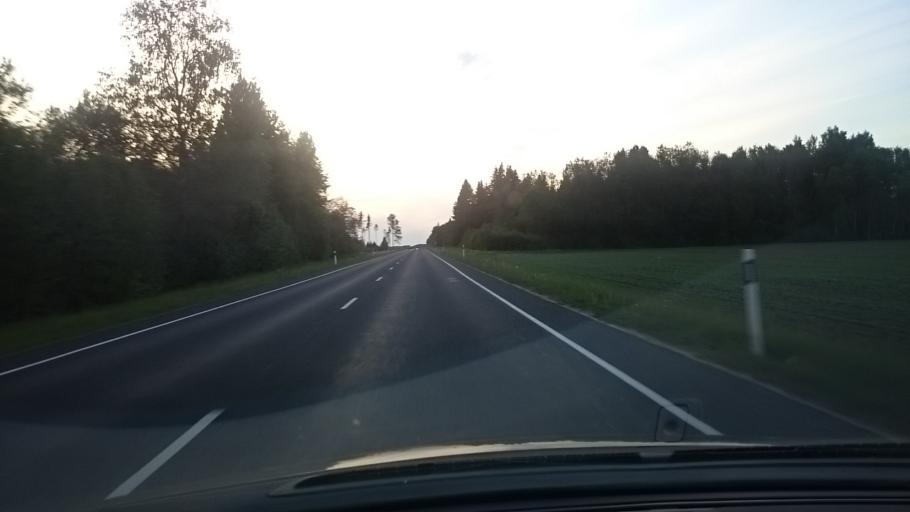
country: EE
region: Viljandimaa
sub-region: Vohma linn
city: Vohma
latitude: 58.7143
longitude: 25.6131
